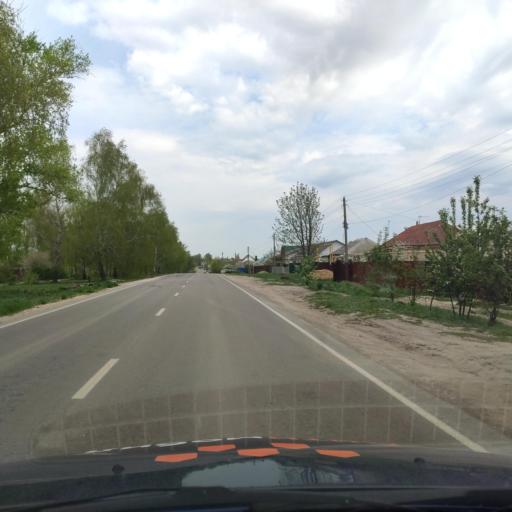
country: RU
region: Voronezj
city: Podgornoye
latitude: 51.8805
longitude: 39.1729
